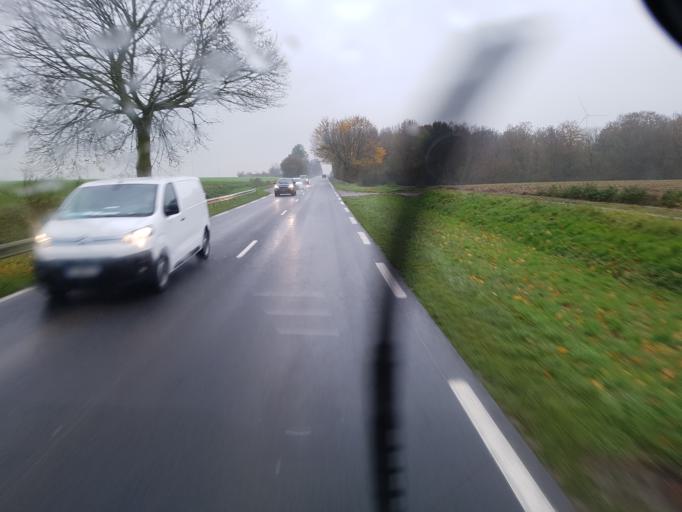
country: FR
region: Picardie
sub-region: Departement de l'Aisne
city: Saint-Quentin
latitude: 49.8828
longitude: 3.2672
